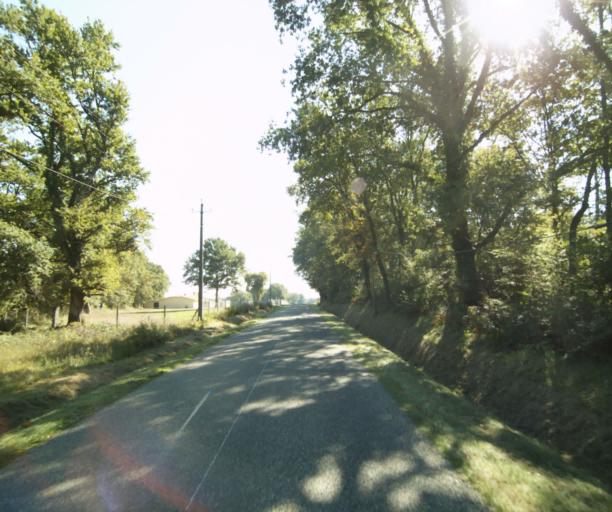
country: FR
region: Aquitaine
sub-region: Departement des Landes
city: Gabarret
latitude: 43.9549
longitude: -0.0160
